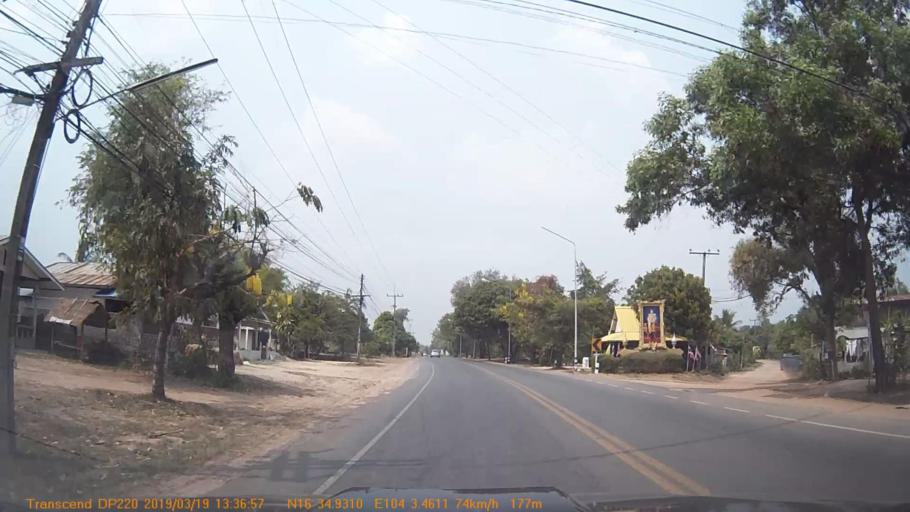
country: TH
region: Kalasin
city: Kuchinarai
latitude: 16.5827
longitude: 104.0577
